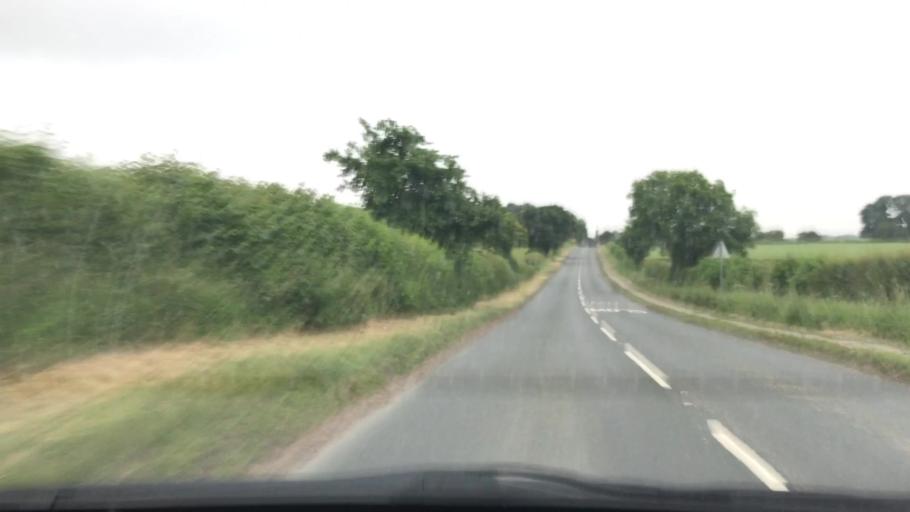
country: GB
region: England
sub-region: City and Borough of Leeds
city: Wetherby
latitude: 53.9560
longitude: -1.4010
